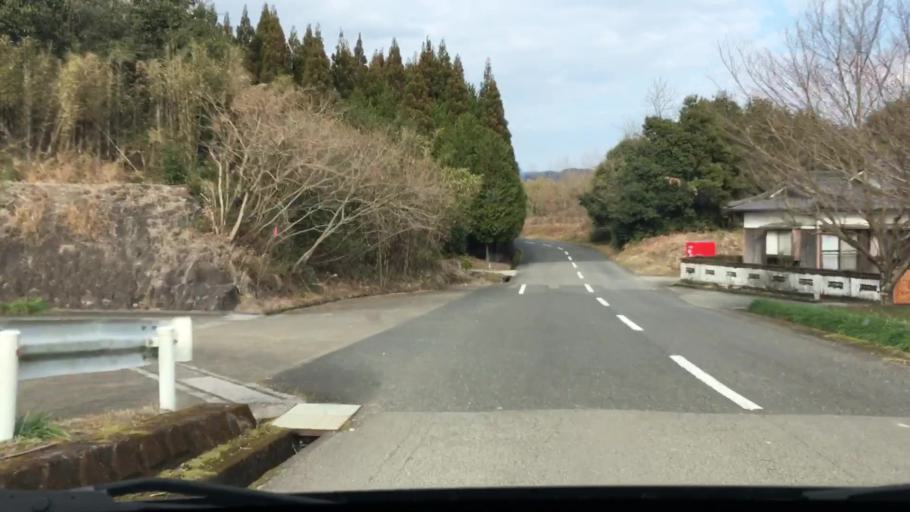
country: JP
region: Miyazaki
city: Nichinan
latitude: 31.6186
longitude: 131.3358
